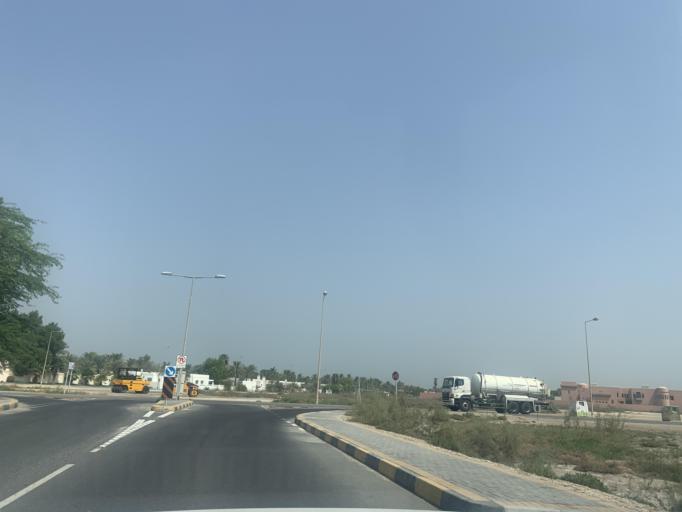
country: BH
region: Central Governorate
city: Madinat Hamad
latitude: 26.1573
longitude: 50.4676
